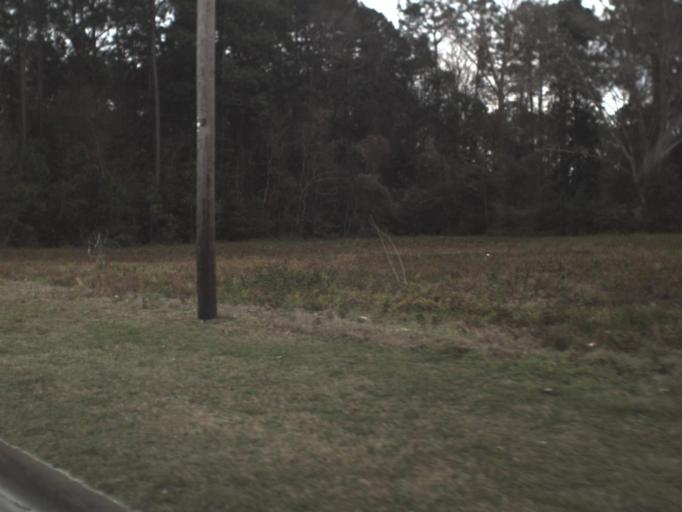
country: US
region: Florida
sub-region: Bay County
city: Cedar Grove
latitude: 30.1748
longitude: -85.6043
